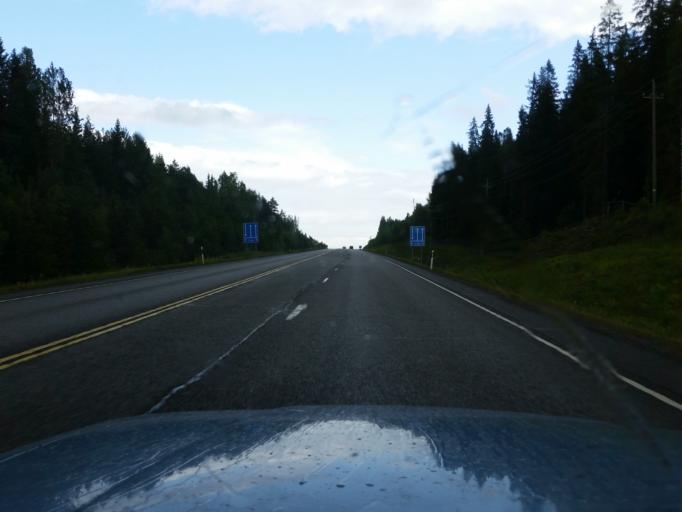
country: FI
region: Southern Savonia
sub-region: Mikkeli
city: Maentyharju
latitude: 61.5492
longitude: 26.9296
